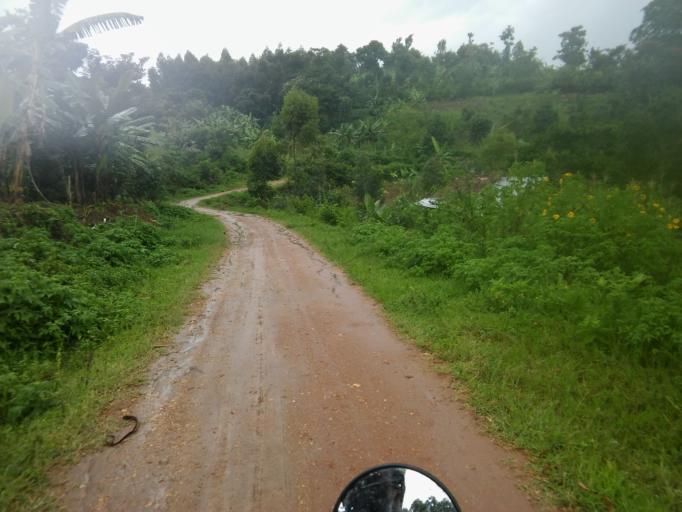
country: UG
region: Eastern Region
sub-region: Bududa District
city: Bududa
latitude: 1.0006
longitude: 34.2428
